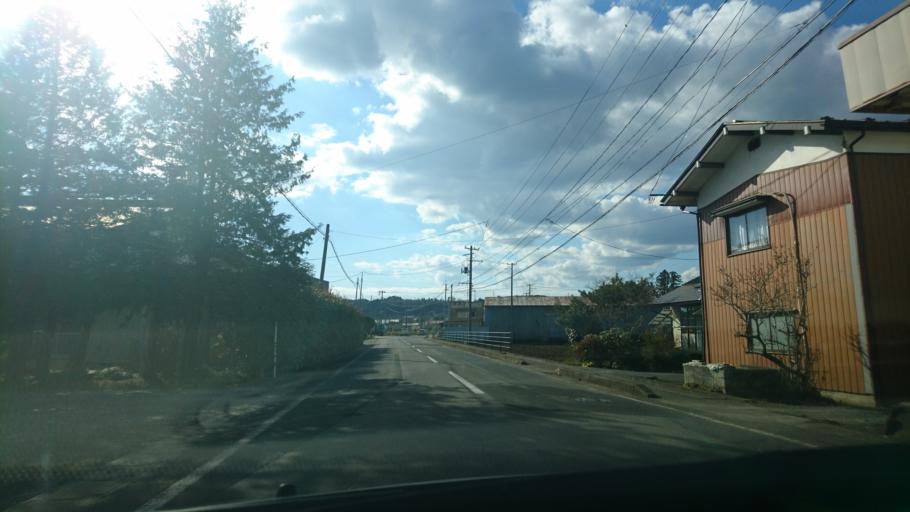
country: JP
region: Iwate
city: Mizusawa
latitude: 39.0448
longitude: 141.1344
